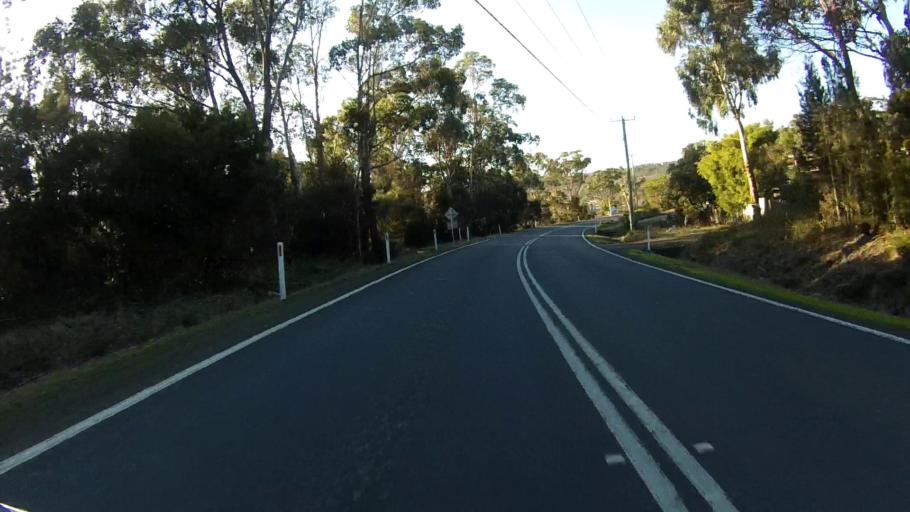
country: AU
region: Tasmania
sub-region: Clarence
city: Sandford
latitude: -43.0349
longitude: 147.8647
